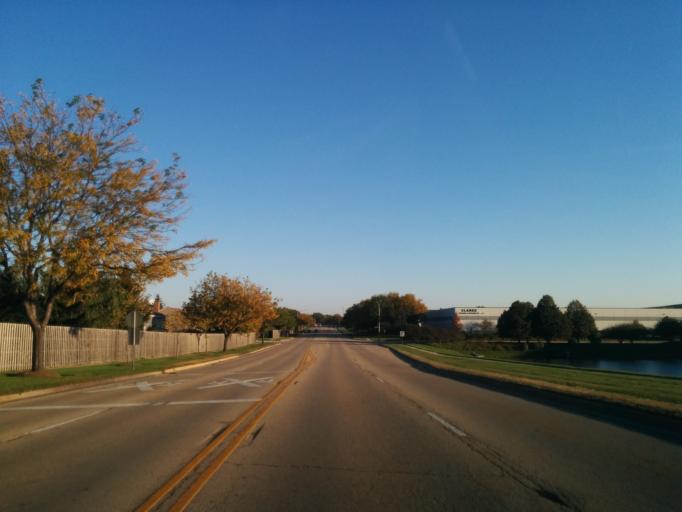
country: US
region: Illinois
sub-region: DuPage County
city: Carol Stream
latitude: 41.9473
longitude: -88.1502
